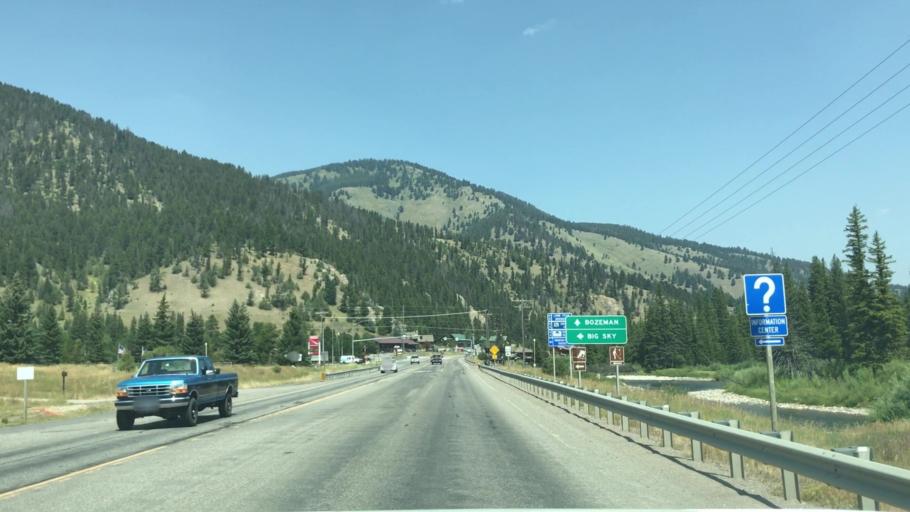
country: US
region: Montana
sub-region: Gallatin County
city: Big Sky
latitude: 45.2625
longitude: -111.2538
